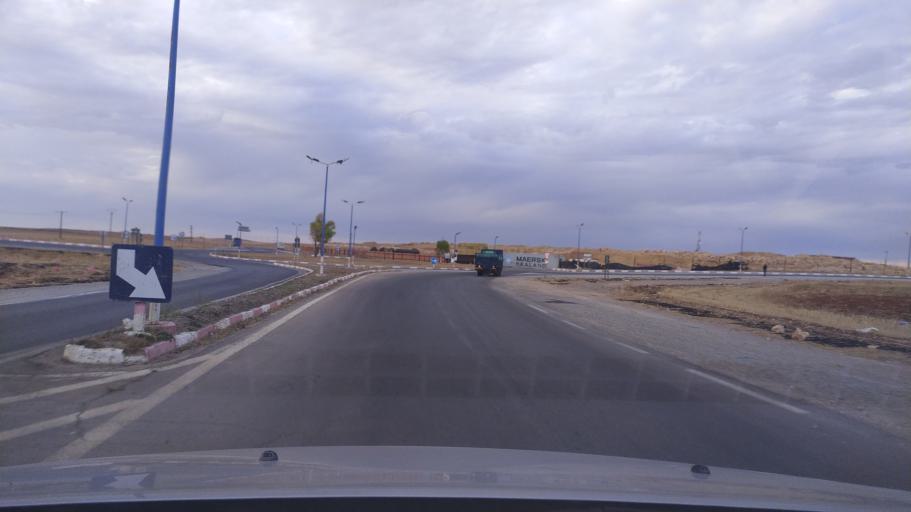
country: DZ
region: Tiaret
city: Frenda
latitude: 34.9913
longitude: 1.1304
